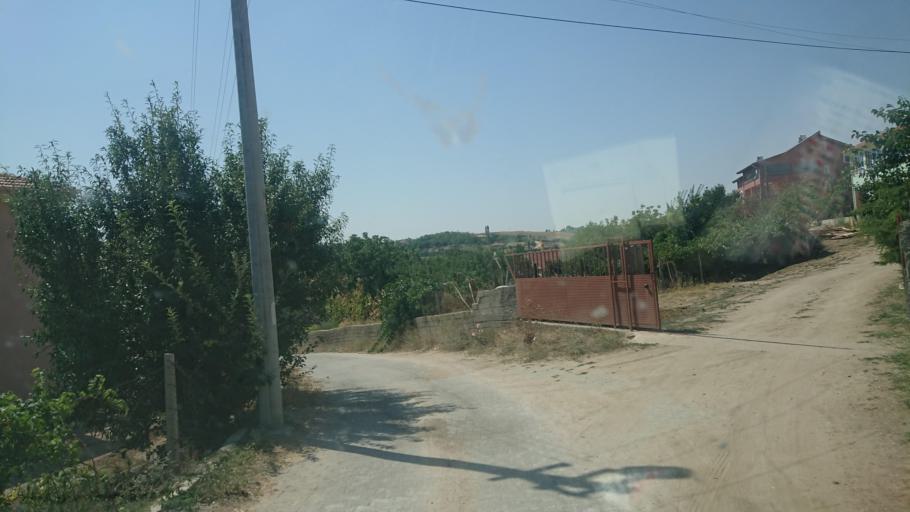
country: TR
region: Aksaray
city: Agacoren
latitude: 38.8231
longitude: 33.9573
